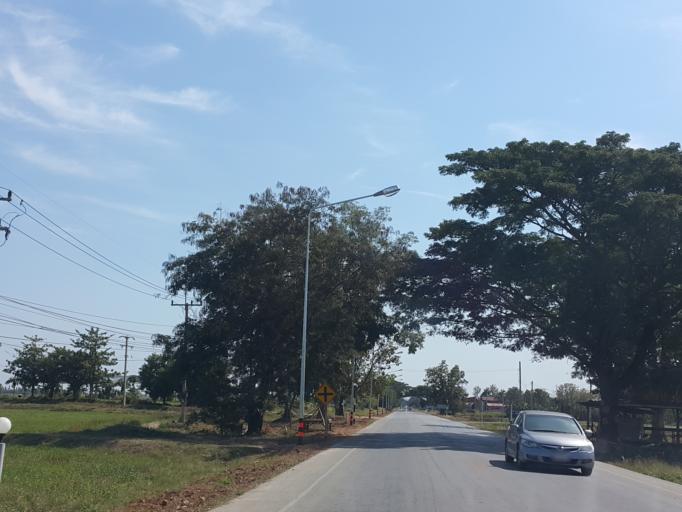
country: TH
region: Sukhothai
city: Thung Saliam
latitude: 17.3421
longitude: 99.6017
